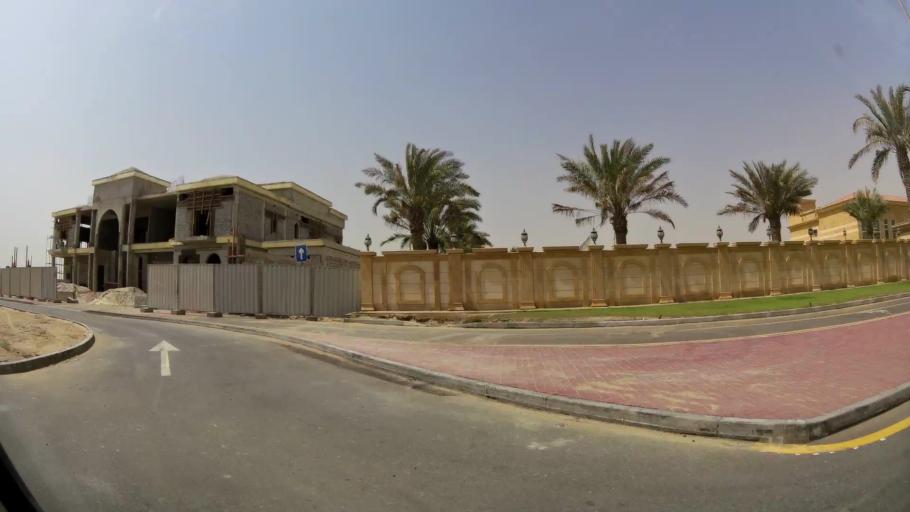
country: AE
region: Ash Shariqah
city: Sharjah
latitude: 25.2601
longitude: 55.4780
